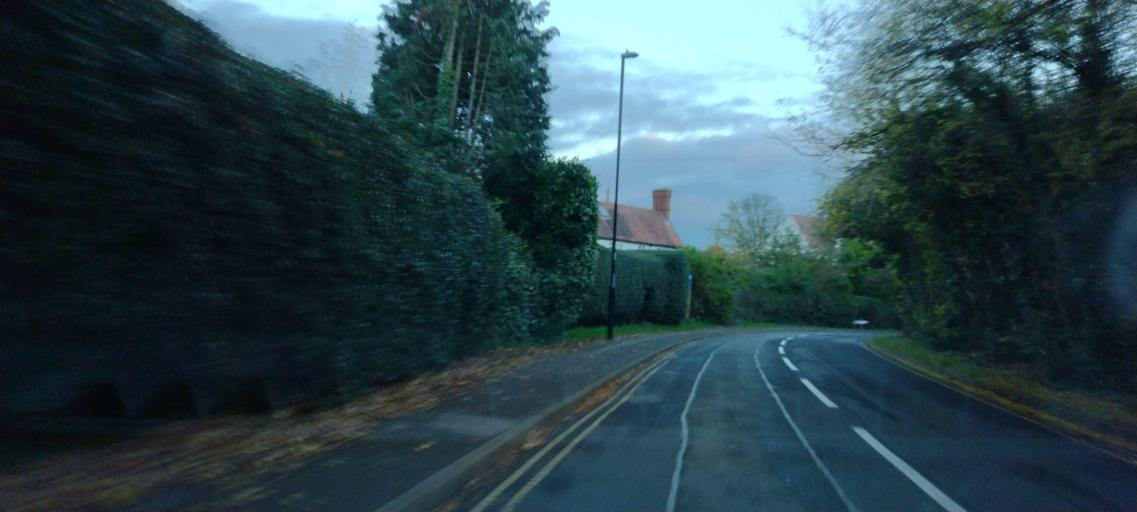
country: GB
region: England
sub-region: Coventry
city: Coventry
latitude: 52.3965
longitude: -1.5350
